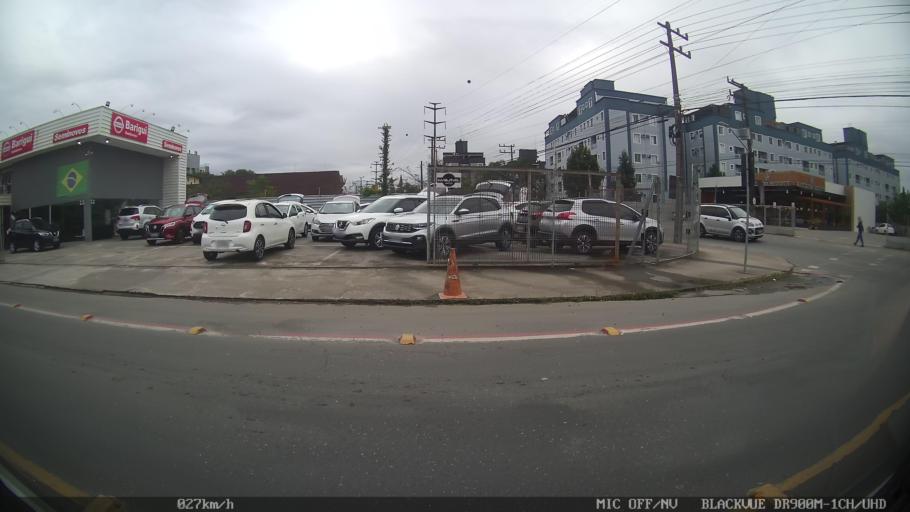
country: BR
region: Santa Catarina
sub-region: Joinville
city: Joinville
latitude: -26.2662
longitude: -48.8598
